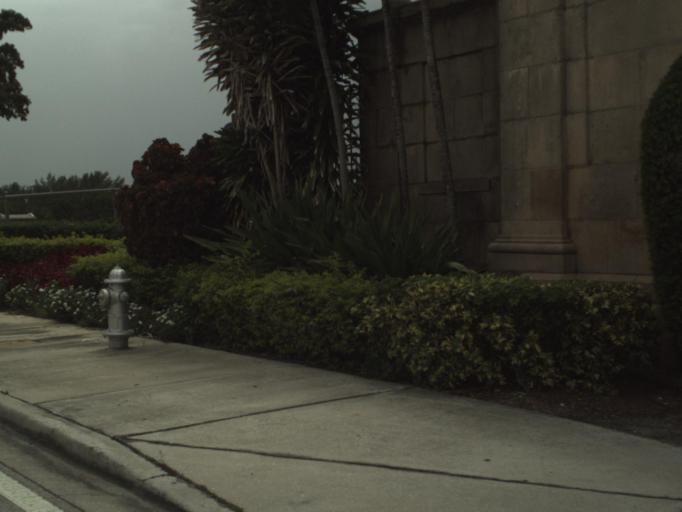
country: US
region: Florida
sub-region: Palm Beach County
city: West Palm Beach
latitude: 26.7022
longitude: -80.0539
